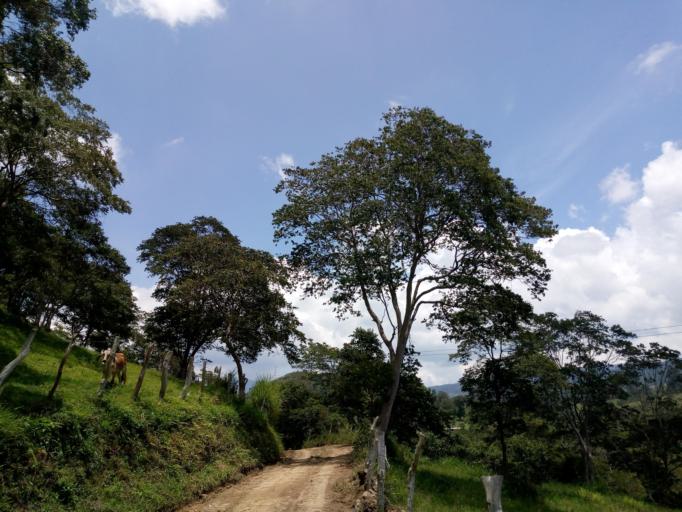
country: CO
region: Boyaca
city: Moniquira
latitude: 5.8692
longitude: -73.5088
